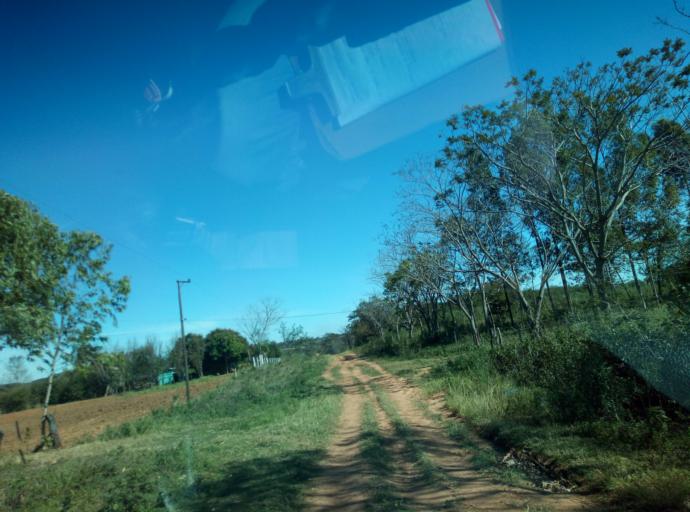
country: PY
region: Caaguazu
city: Doctor Cecilio Baez
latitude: -25.1789
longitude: -56.2465
